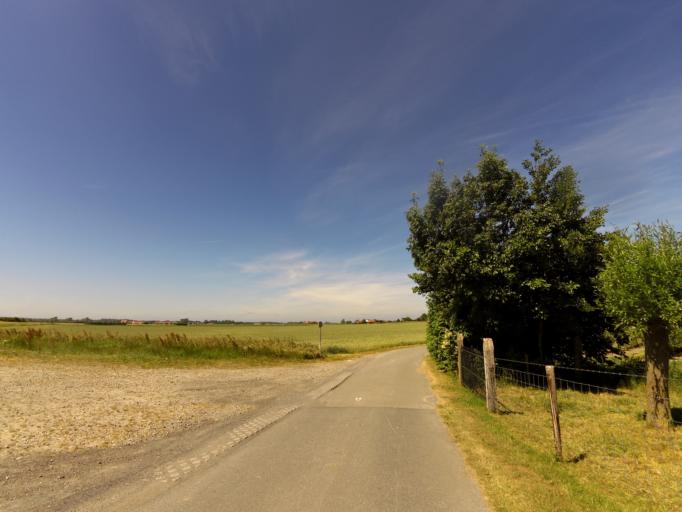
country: NL
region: Zeeland
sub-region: Gemeente Sluis
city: Sluis
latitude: 51.3265
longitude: 3.3667
